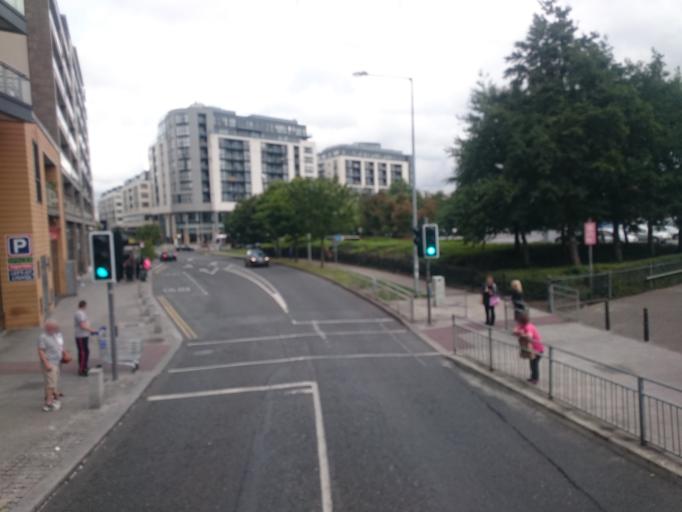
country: IE
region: Leinster
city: Tallaght
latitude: 53.2863
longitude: -6.3751
